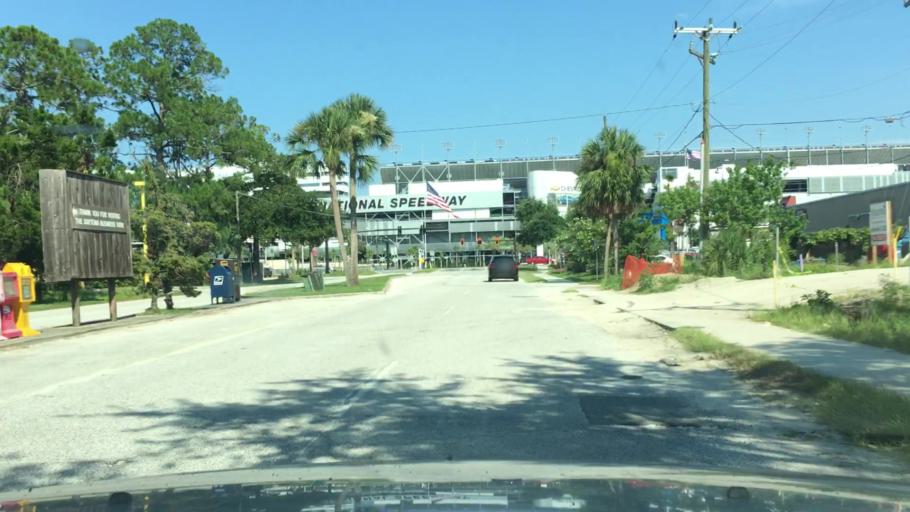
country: US
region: Florida
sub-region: Volusia County
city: Daytona Beach
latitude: 29.1884
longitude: -81.0776
